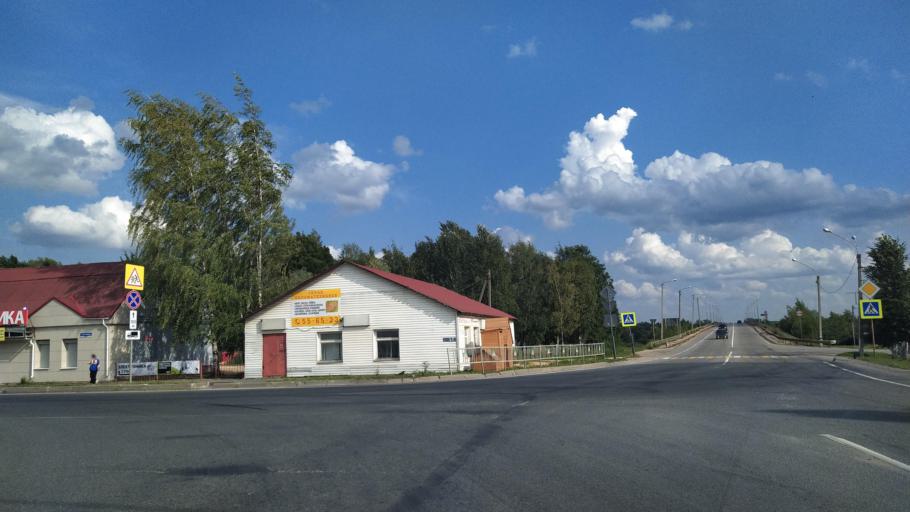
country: RU
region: Novgorod
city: Shimsk
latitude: 58.2092
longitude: 30.7192
